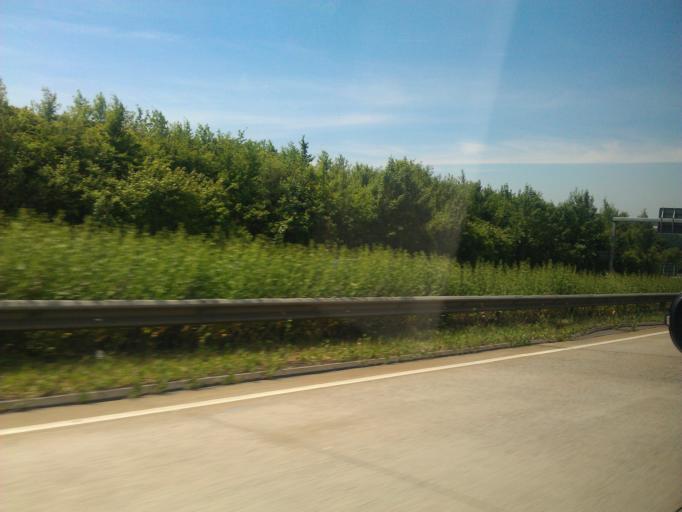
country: DE
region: Rheinland-Pfalz
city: Breitscheid
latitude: 50.6123
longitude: 7.4261
